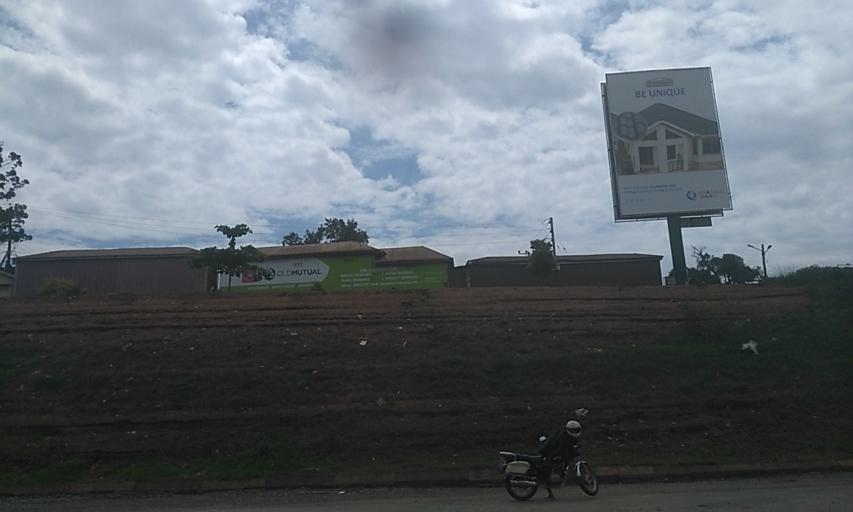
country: UG
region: Central Region
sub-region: Wakiso District
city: Kireka
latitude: 0.3694
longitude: 32.6251
